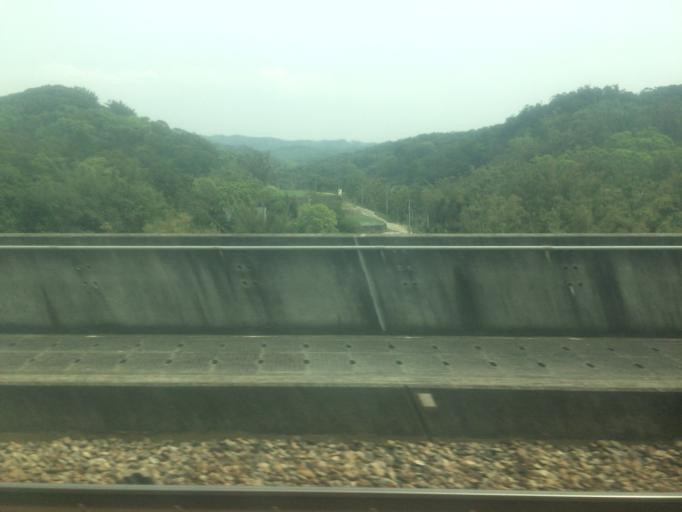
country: TW
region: Taiwan
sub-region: Miaoli
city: Miaoli
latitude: 24.5121
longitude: 120.7300
